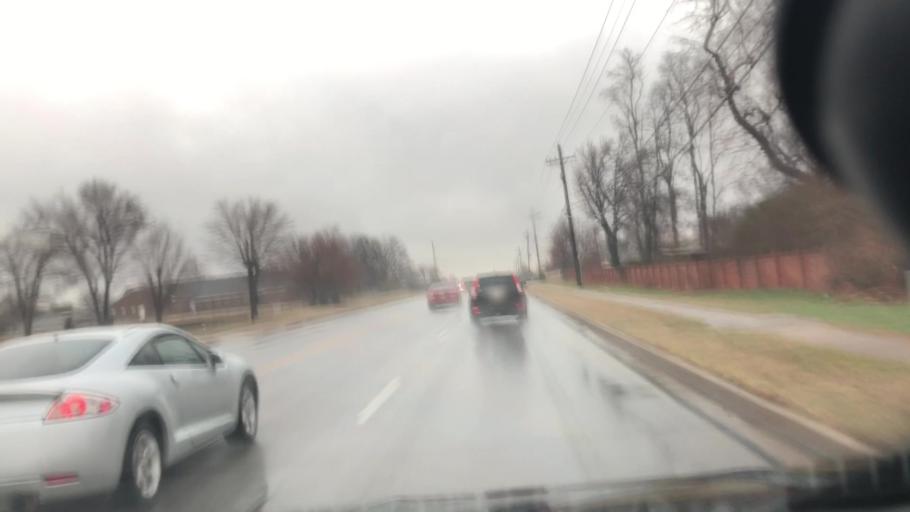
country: US
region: Oklahoma
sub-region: Rogers County
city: Catoosa
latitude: 36.1425
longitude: -95.8333
